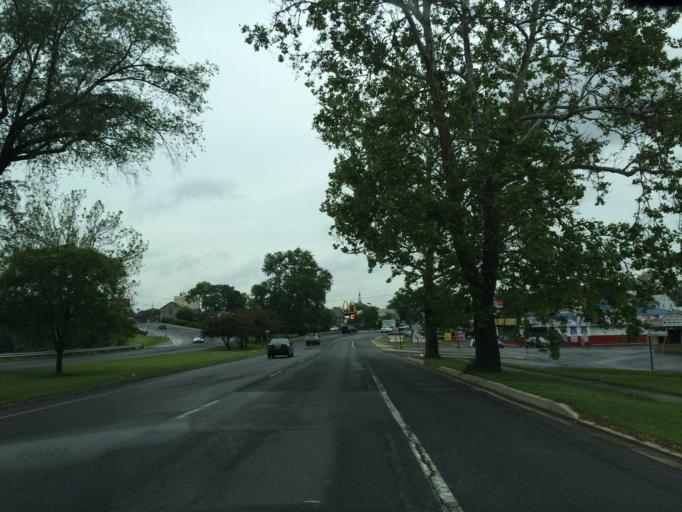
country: US
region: Maryland
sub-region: Washington County
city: Hagerstown
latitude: 39.6387
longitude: -77.7114
